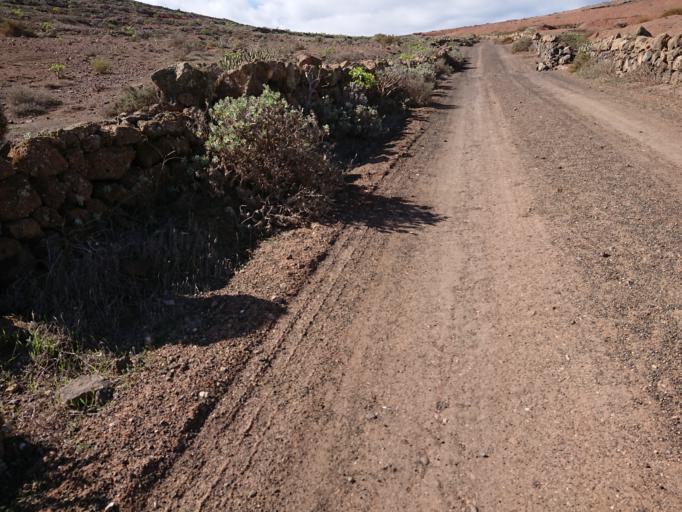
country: ES
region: Canary Islands
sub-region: Provincia de Las Palmas
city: Haria
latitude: 29.1456
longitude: -13.5162
